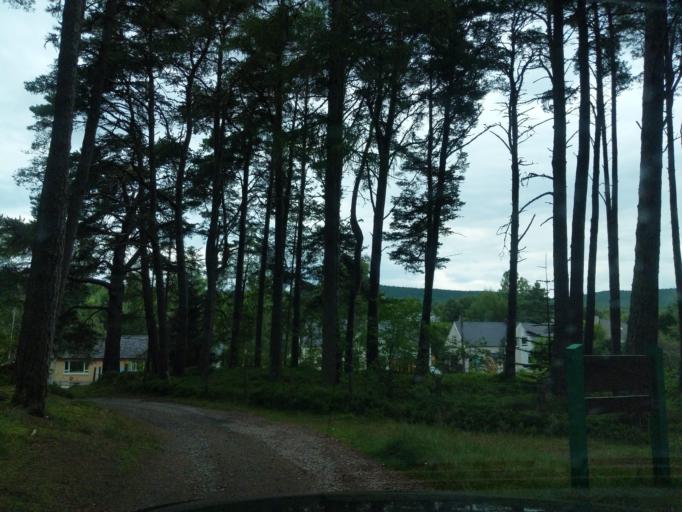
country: GB
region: Scotland
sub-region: Highland
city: Aviemore
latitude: 57.2826
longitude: -3.8193
